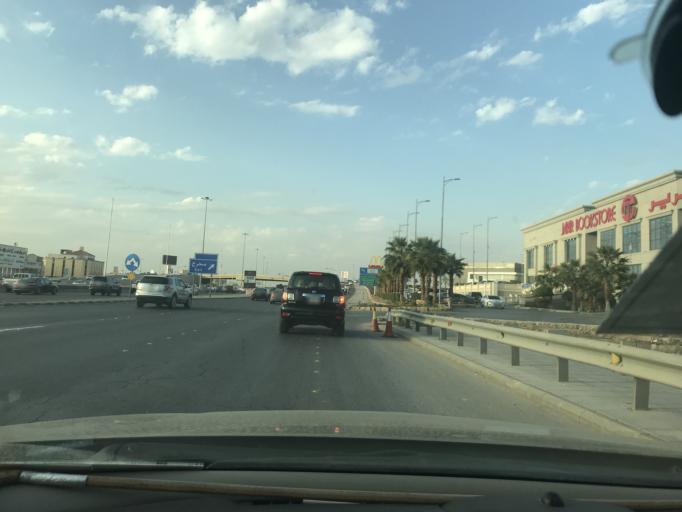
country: SA
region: Ar Riyad
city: Riyadh
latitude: 24.7510
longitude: 46.5838
